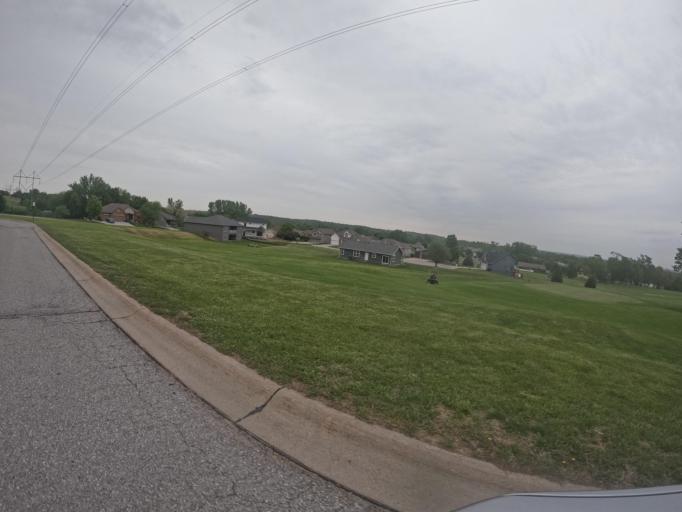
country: US
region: Nebraska
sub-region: Sarpy County
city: Offutt Air Force Base
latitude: 41.0462
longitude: -95.9591
